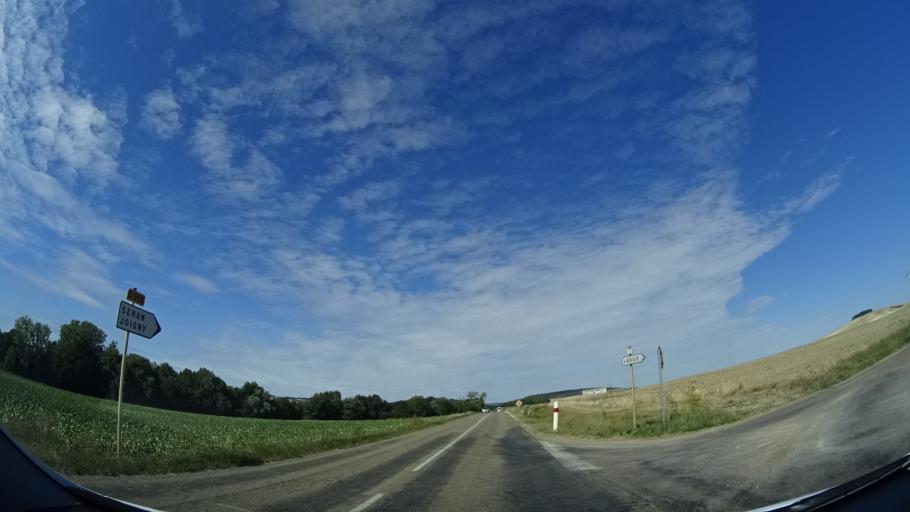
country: FR
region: Bourgogne
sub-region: Departement de l'Yonne
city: Aillant-sur-Tholon
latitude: 47.8908
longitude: 3.3540
